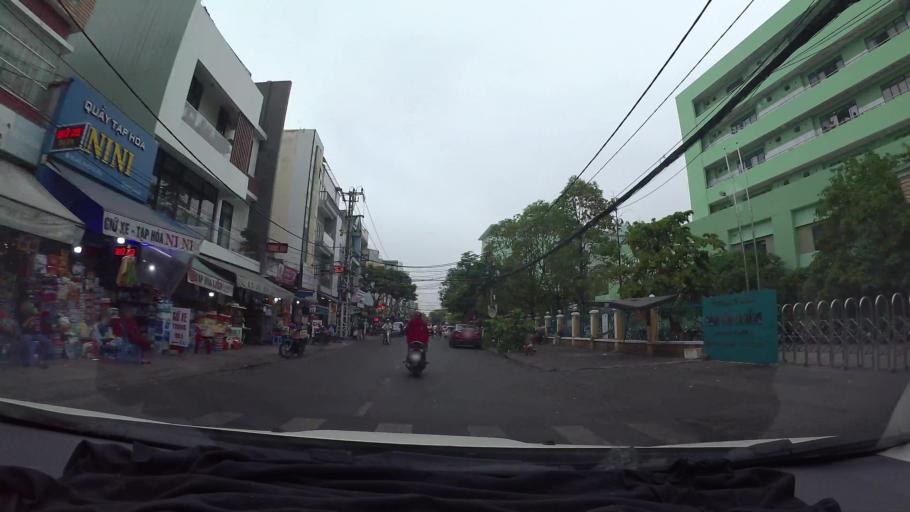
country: VN
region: Da Nang
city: Da Nang
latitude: 16.0720
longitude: 108.2157
